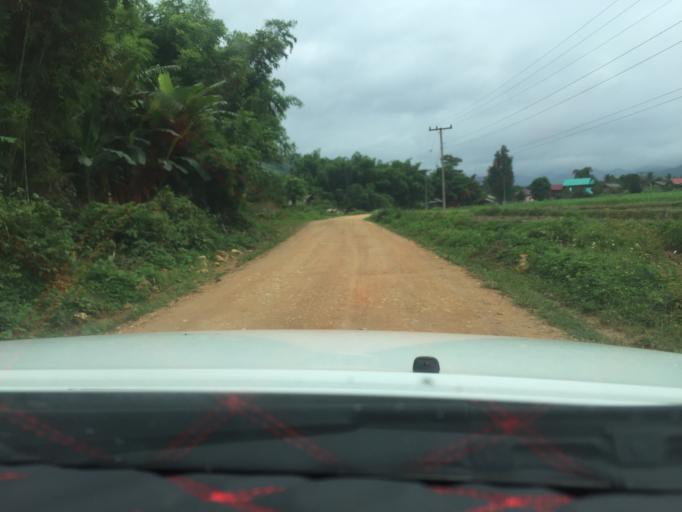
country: TH
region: Phayao
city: Phu Sang
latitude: 19.6818
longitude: 100.5027
